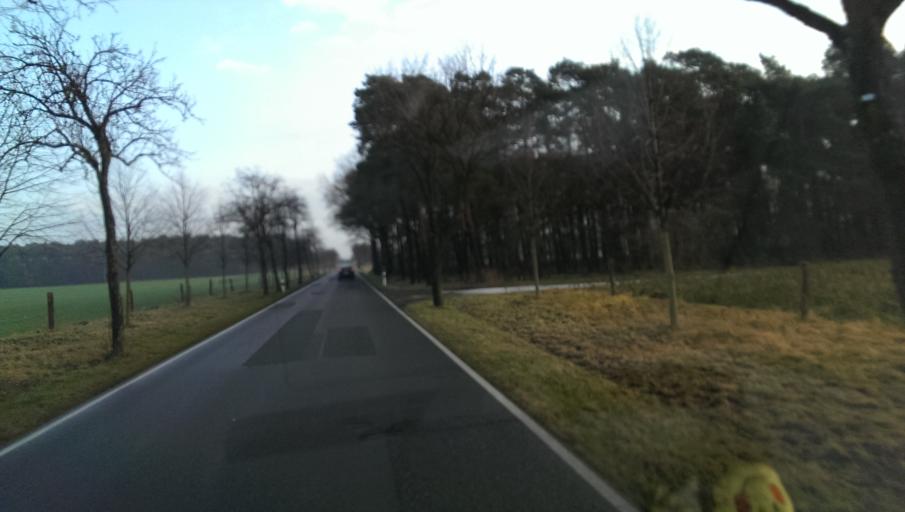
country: DE
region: Brandenburg
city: Merzdorf
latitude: 51.4106
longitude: 13.4894
